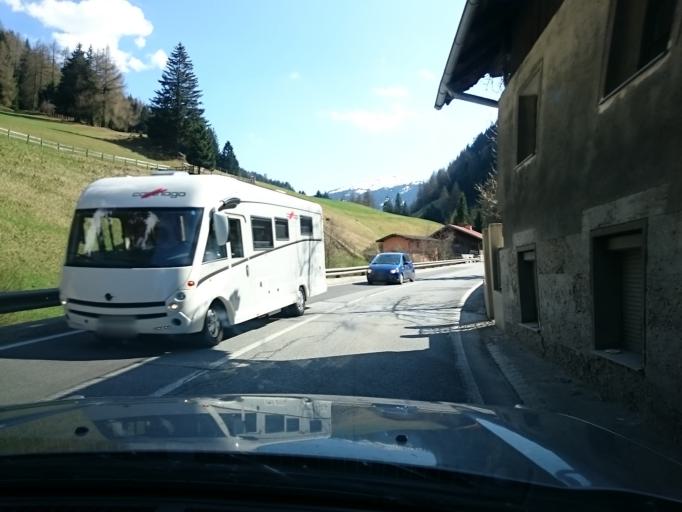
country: AT
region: Tyrol
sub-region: Politischer Bezirk Innsbruck Land
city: Gries am Brenner
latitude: 47.0570
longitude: 11.4855
